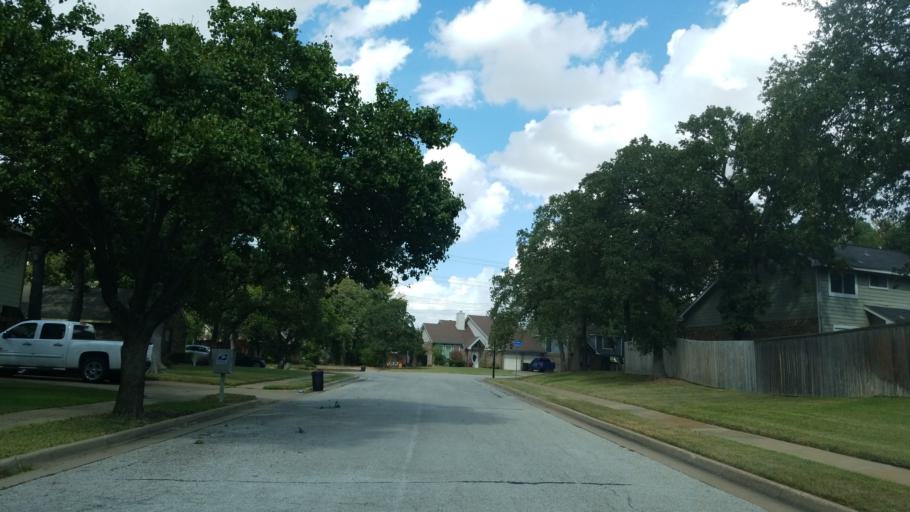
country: US
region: Texas
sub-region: Tarrant County
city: Euless
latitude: 32.8689
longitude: -97.0766
